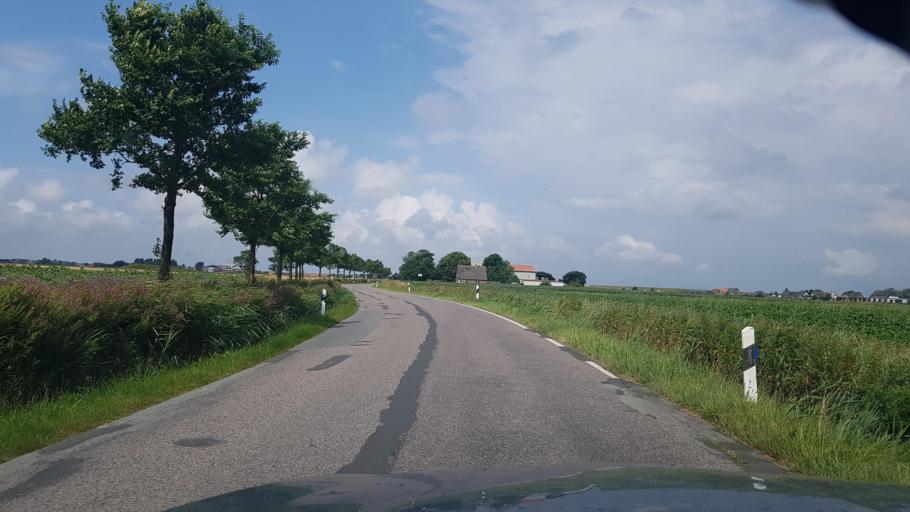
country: DE
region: Schleswig-Holstein
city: Elisabeth-Sophien-Koog
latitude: 54.4992
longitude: 8.8417
